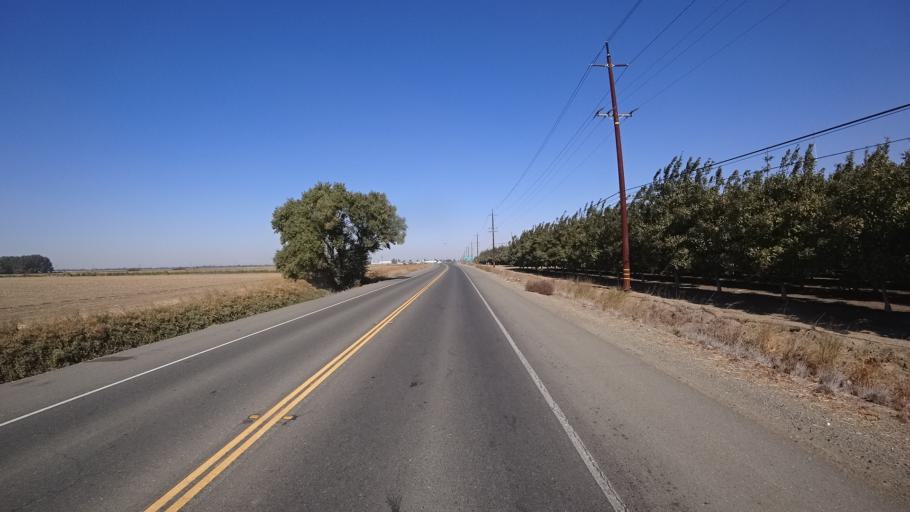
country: US
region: California
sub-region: Yolo County
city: Davis
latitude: 38.5856
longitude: -121.7303
